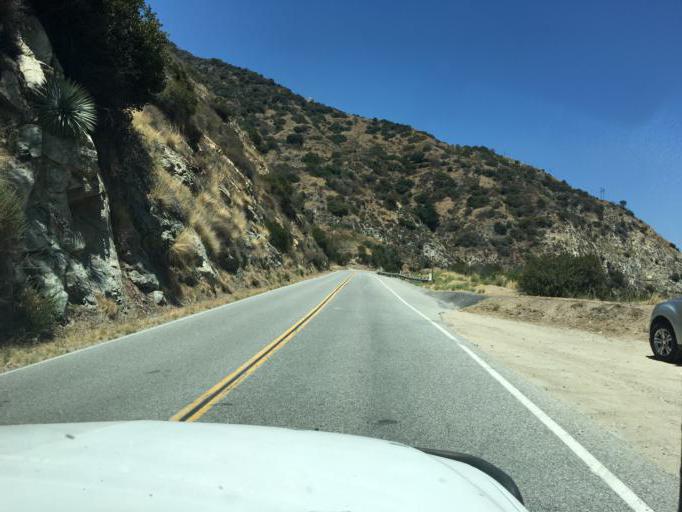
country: US
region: California
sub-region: Los Angeles County
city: Glendora
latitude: 34.1731
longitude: -117.8869
